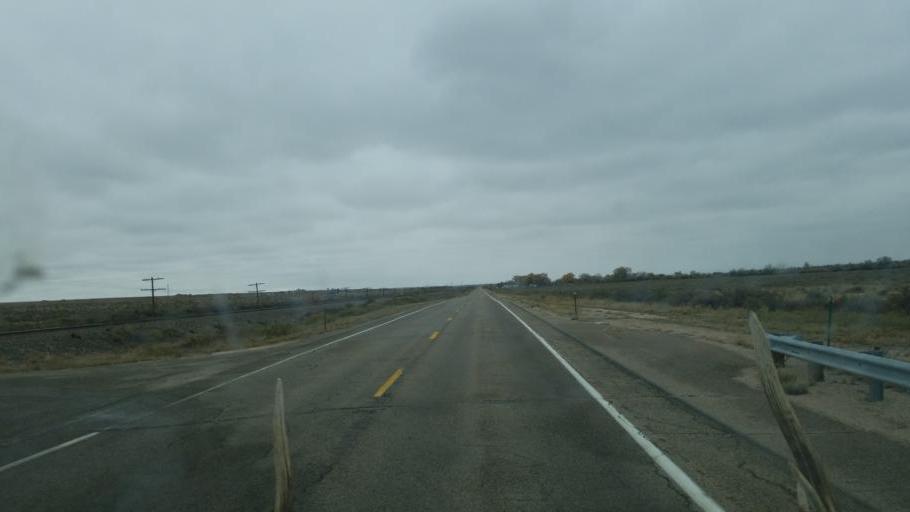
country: US
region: Colorado
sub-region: Otero County
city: Fowler
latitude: 38.2530
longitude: -104.2927
